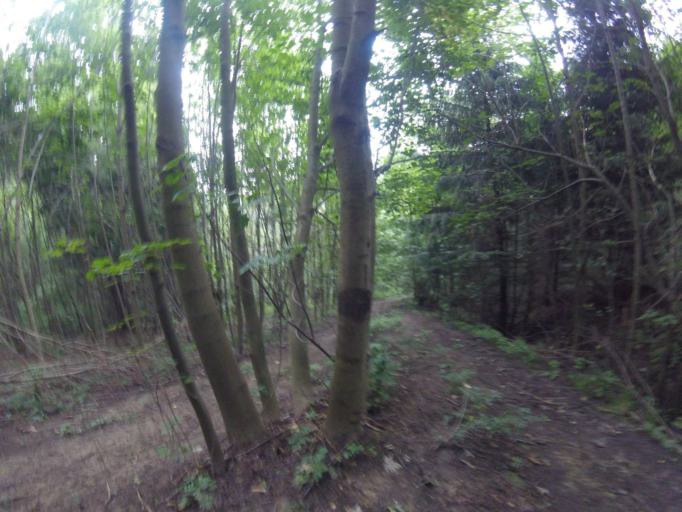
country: SK
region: Zilinsky
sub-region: Okres Zilina
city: Terchova
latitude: 49.2300
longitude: 19.0150
